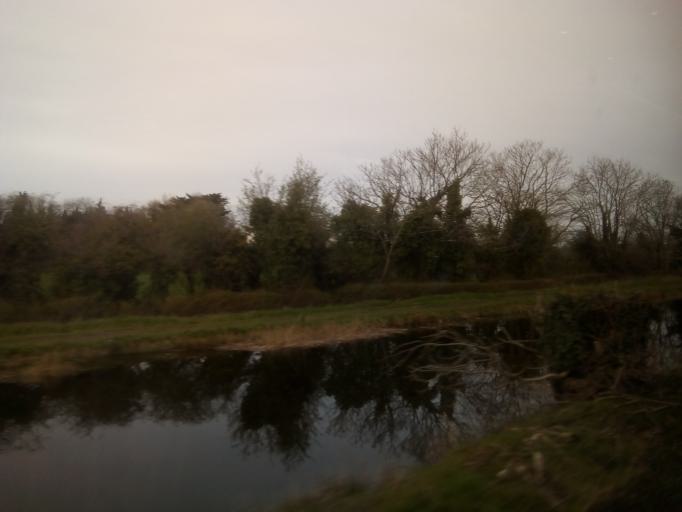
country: IE
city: Confey
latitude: 53.3734
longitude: -6.4764
